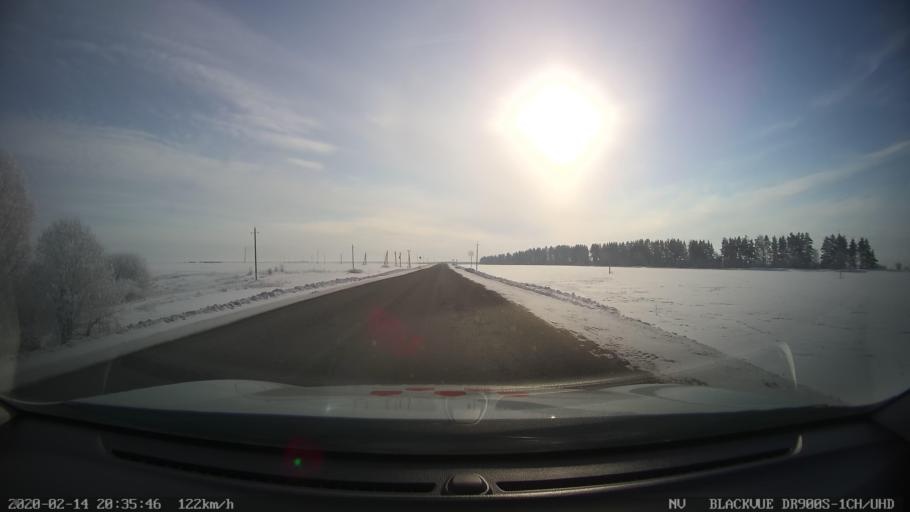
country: RU
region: Tatarstan
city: Kuybyshevskiy Zaton
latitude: 55.3776
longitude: 48.9900
